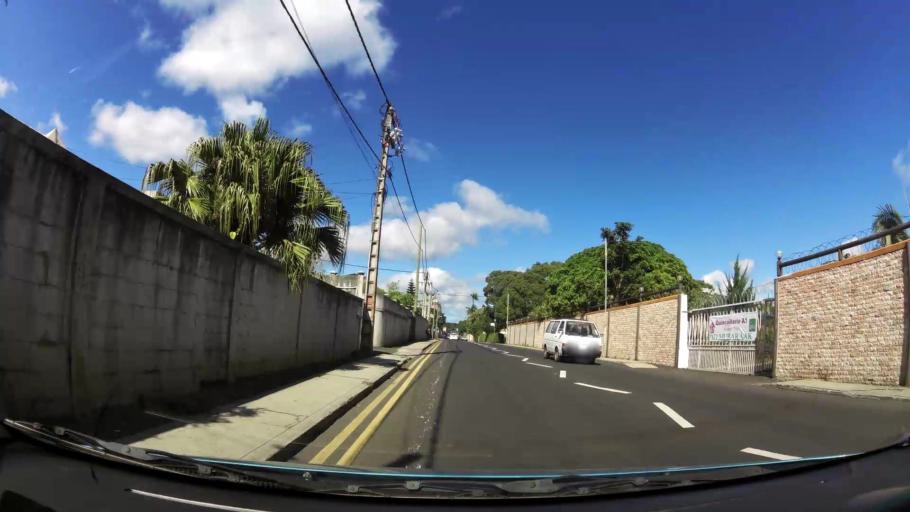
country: MU
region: Plaines Wilhems
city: Vacoas
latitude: -20.3010
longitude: 57.4927
